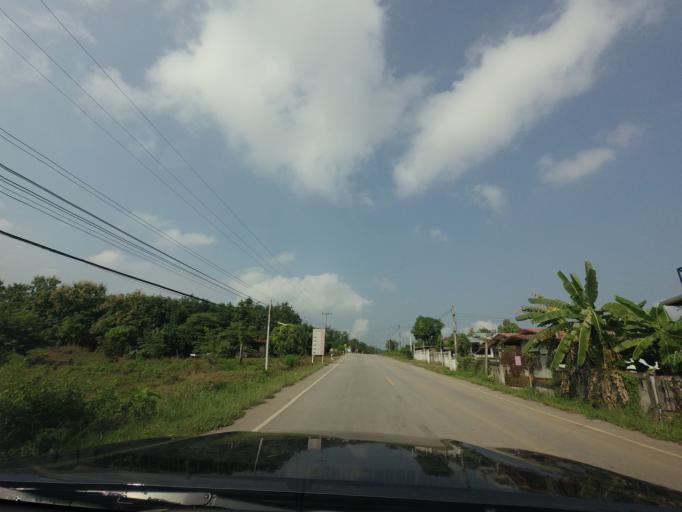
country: TH
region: Loei
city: Chiang Khan
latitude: 17.8904
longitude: 101.6419
